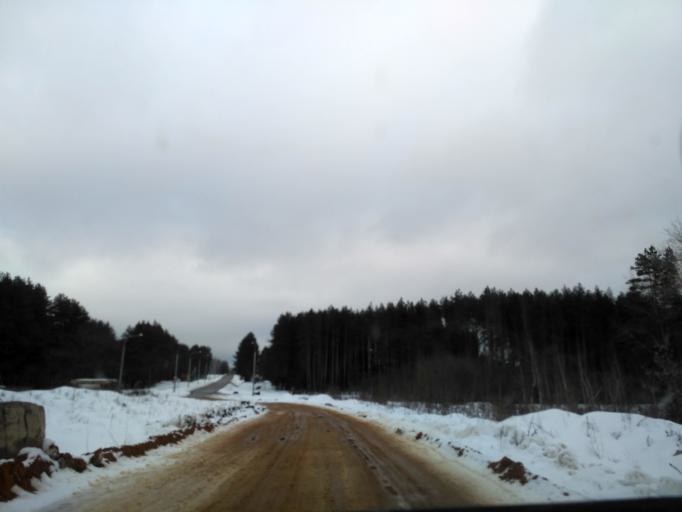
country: BY
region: Minsk
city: Lyeskawka
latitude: 53.9310
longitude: 27.7086
